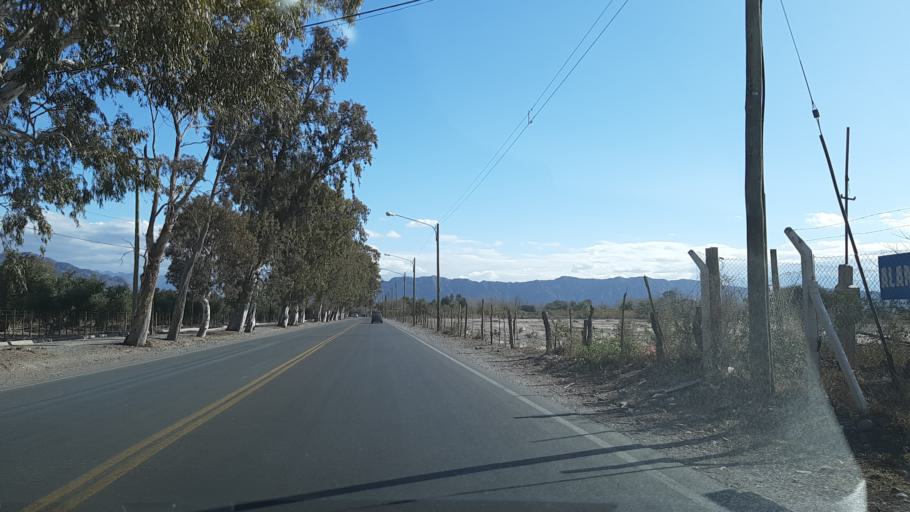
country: AR
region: San Juan
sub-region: Departamento de Rivadavia
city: Rivadavia
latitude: -31.5390
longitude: -68.6084
